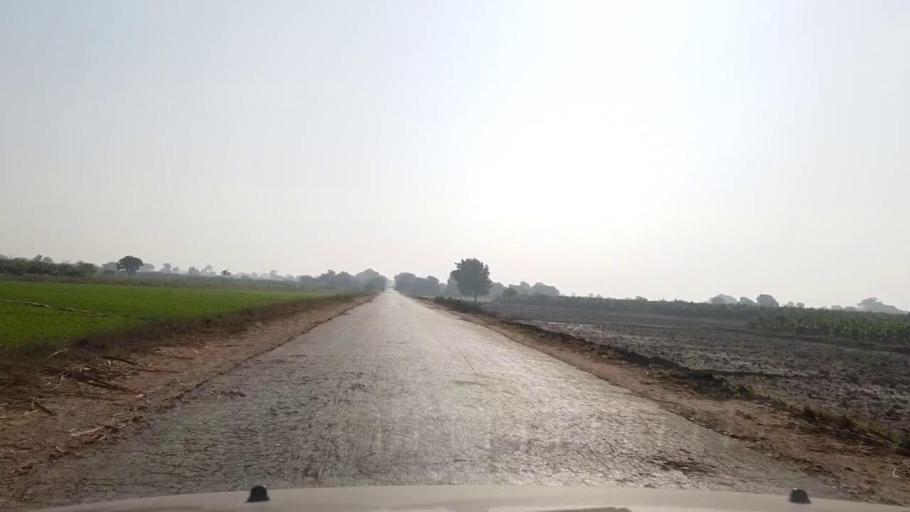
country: PK
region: Sindh
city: Matiari
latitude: 25.5499
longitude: 68.5436
